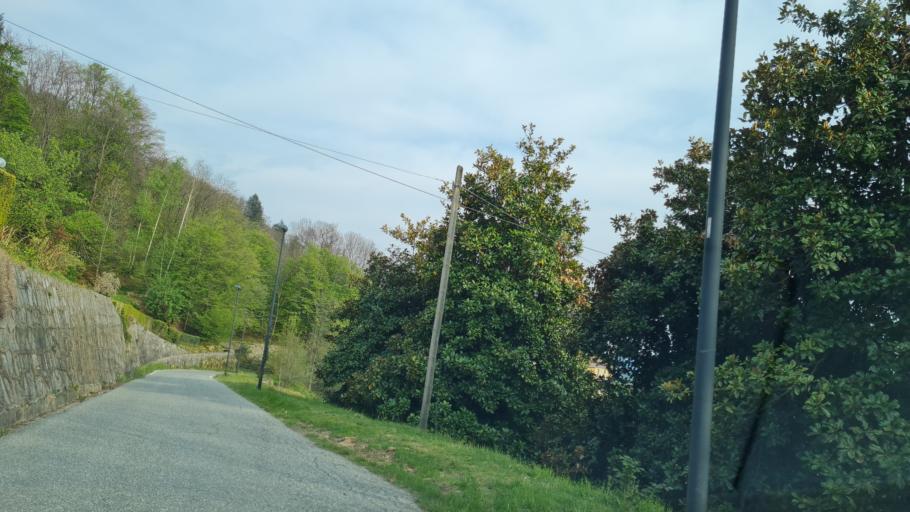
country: IT
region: Piedmont
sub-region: Provincia di Biella
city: Sordevolo
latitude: 45.5792
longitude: 7.9675
